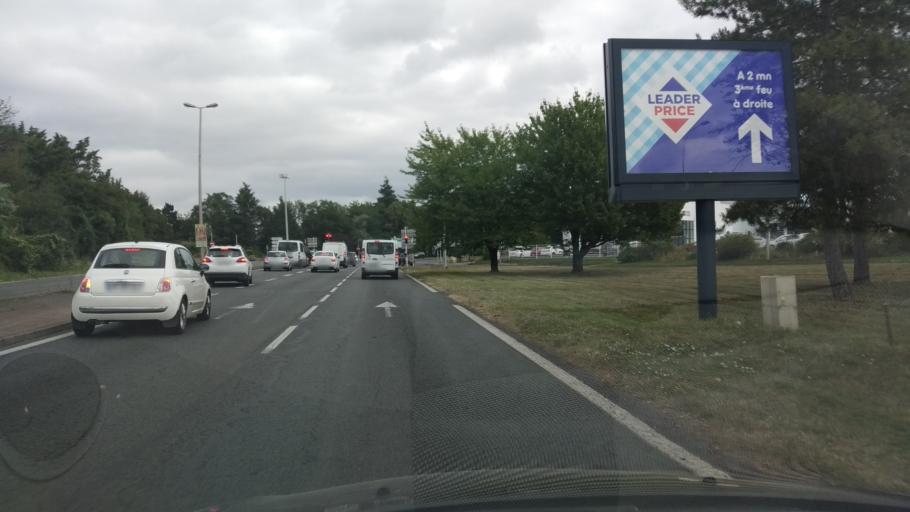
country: FR
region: Poitou-Charentes
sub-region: Departement de la Vienne
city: Saint-Benoit
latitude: 46.5623
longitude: 0.3430
